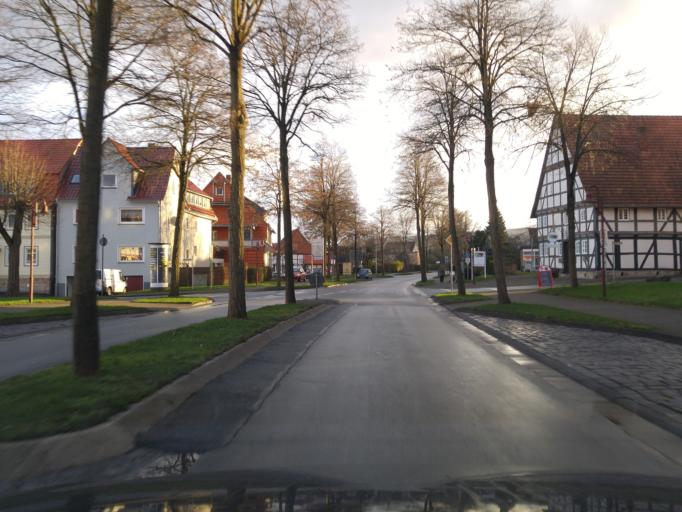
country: DE
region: Lower Saxony
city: Buhren
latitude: 51.4959
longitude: 9.6017
